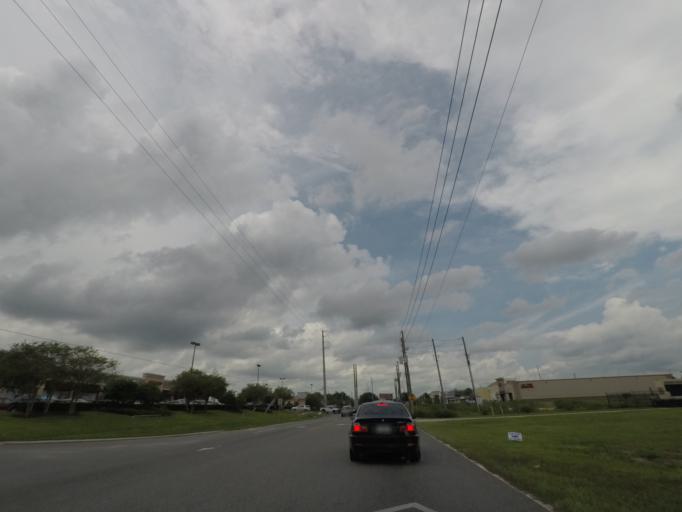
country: US
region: Florida
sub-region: Polk County
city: Loughman
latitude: 28.2572
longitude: -81.5906
